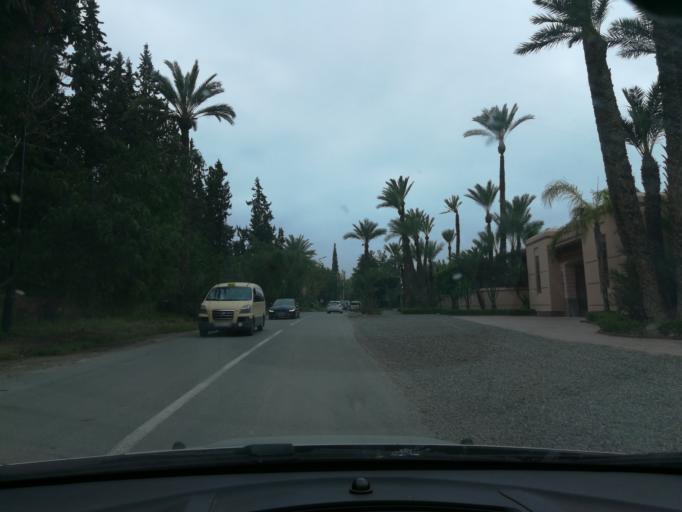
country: MA
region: Marrakech-Tensift-Al Haouz
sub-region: Marrakech
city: Marrakesh
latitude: 31.6558
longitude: -7.9734
